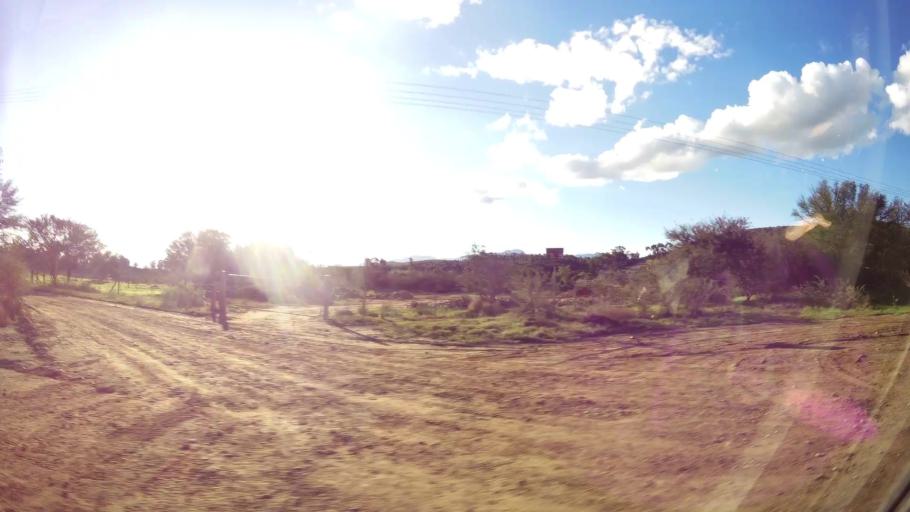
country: ZA
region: Western Cape
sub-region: Eden District Municipality
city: Riversdale
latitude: -34.0894
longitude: 20.9503
